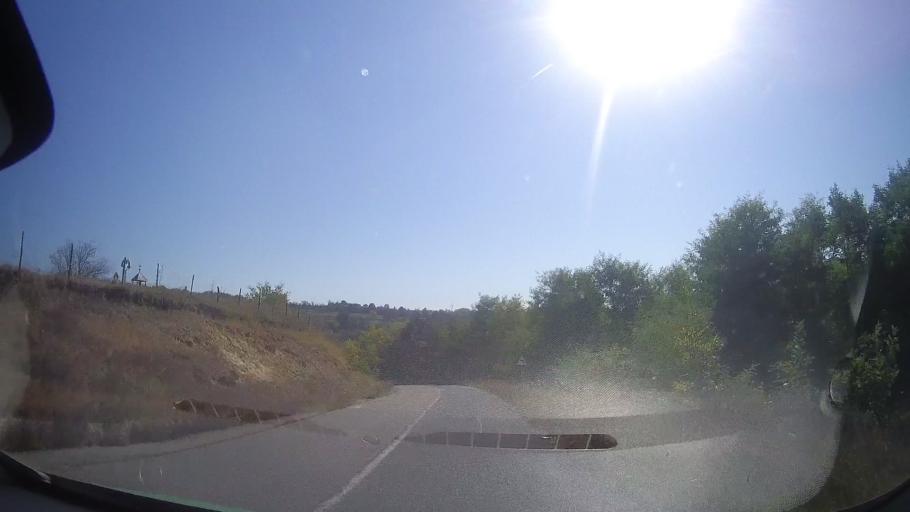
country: RO
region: Timis
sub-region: Comuna Bara
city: Bara
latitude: 45.8937
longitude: 21.9183
